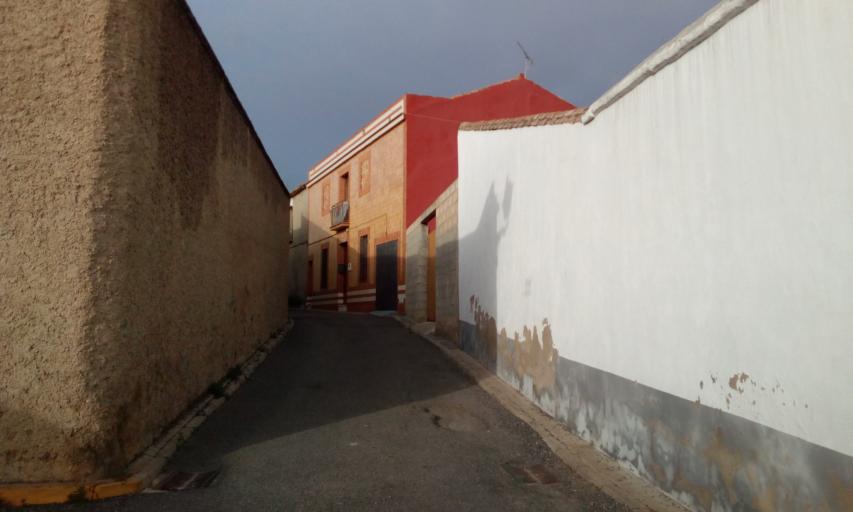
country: ES
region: Andalusia
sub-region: Provincia de Huelva
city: Niebla
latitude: 37.3610
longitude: -6.6792
